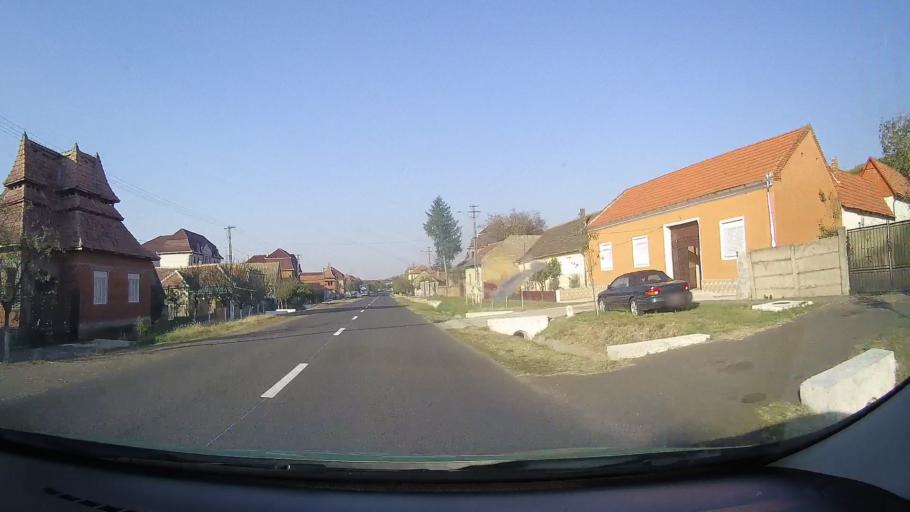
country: RO
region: Arad
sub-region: Comuna Covasint
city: Covasint
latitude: 46.1940
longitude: 21.6063
